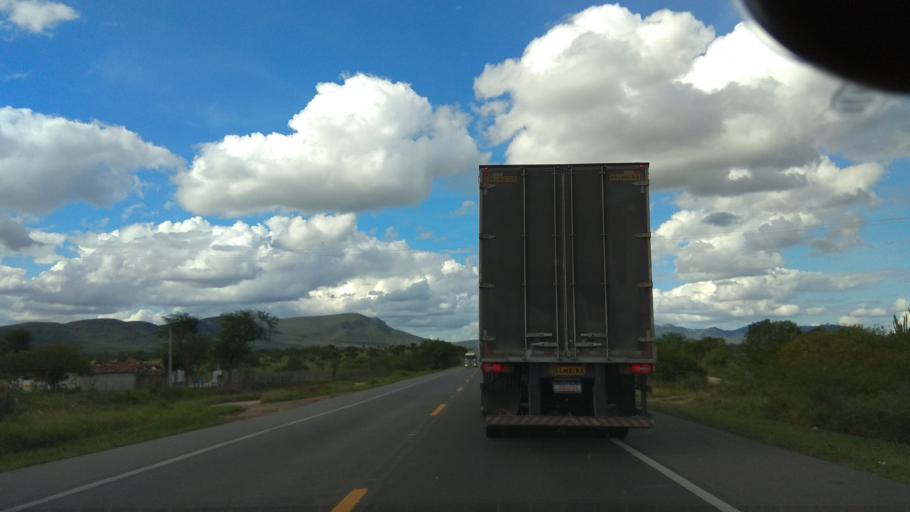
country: BR
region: Bahia
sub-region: Castro Alves
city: Castro Alves
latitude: -12.6766
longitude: -39.6628
